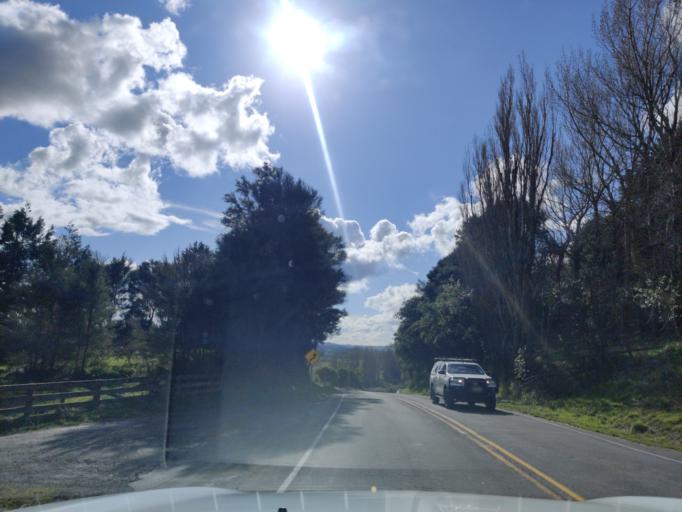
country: NZ
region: Manawatu-Wanganui
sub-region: Palmerston North City
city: Palmerston North
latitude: -40.2838
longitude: 175.7717
